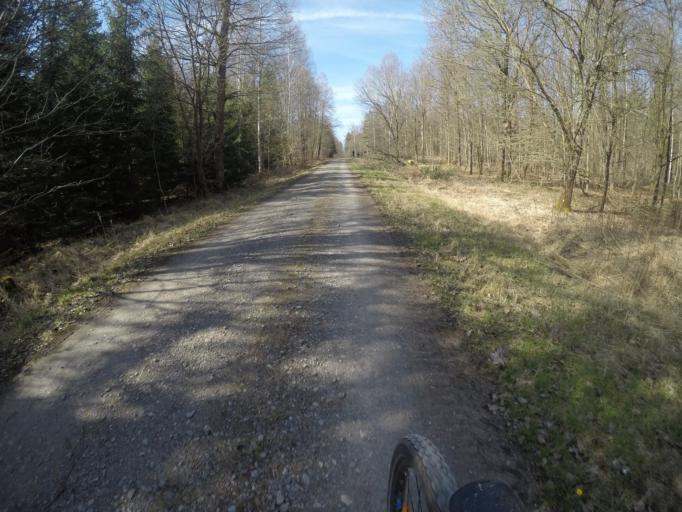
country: DE
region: Baden-Wuerttemberg
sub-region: Regierungsbezirk Stuttgart
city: Gerlingen
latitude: 48.7658
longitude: 9.0753
